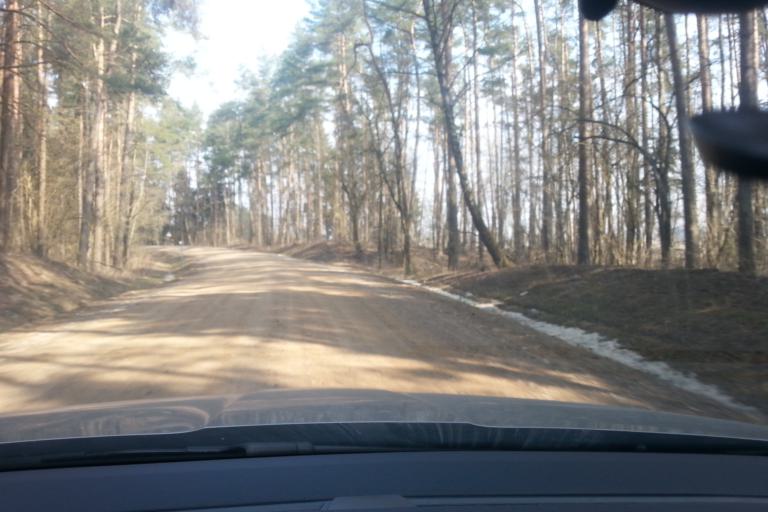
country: LT
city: Trakai
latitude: 54.5787
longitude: 24.9725
